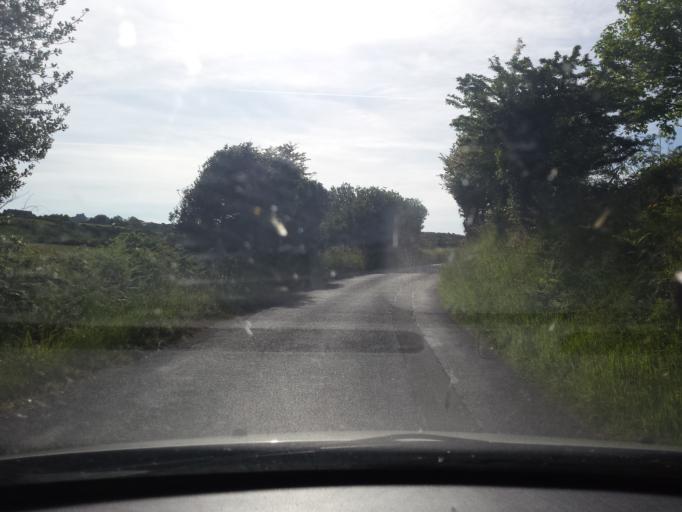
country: FR
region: Lower Normandy
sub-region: Departement de la Manche
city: Beaumont-Hague
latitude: 49.6874
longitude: -1.9270
